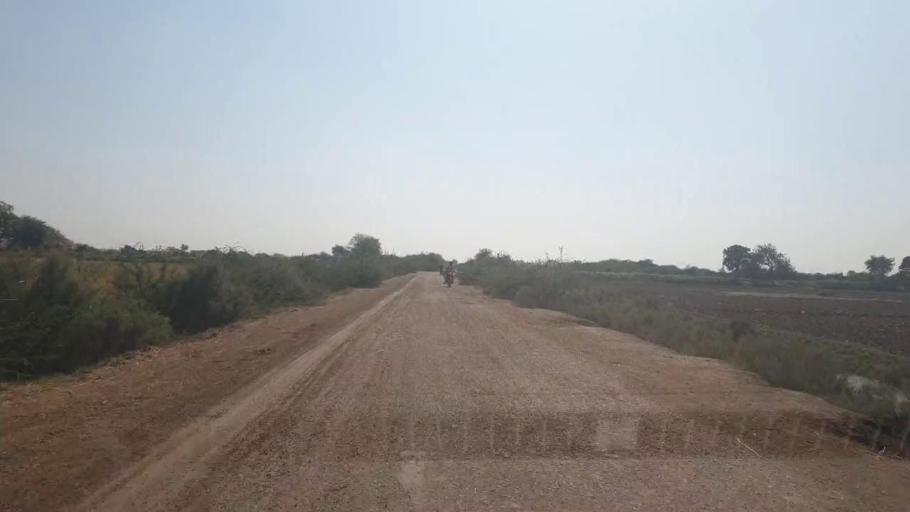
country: PK
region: Sindh
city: Badin
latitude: 24.5673
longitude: 68.8459
